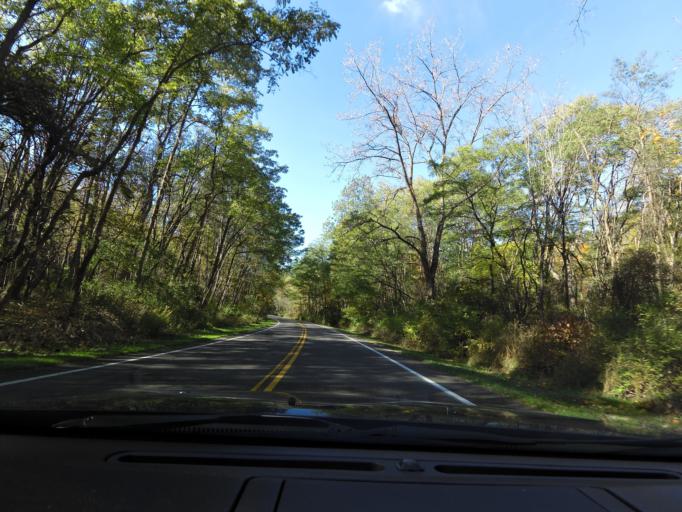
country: US
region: New York
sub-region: Wyoming County
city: Perry
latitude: 42.6974
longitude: -77.9506
